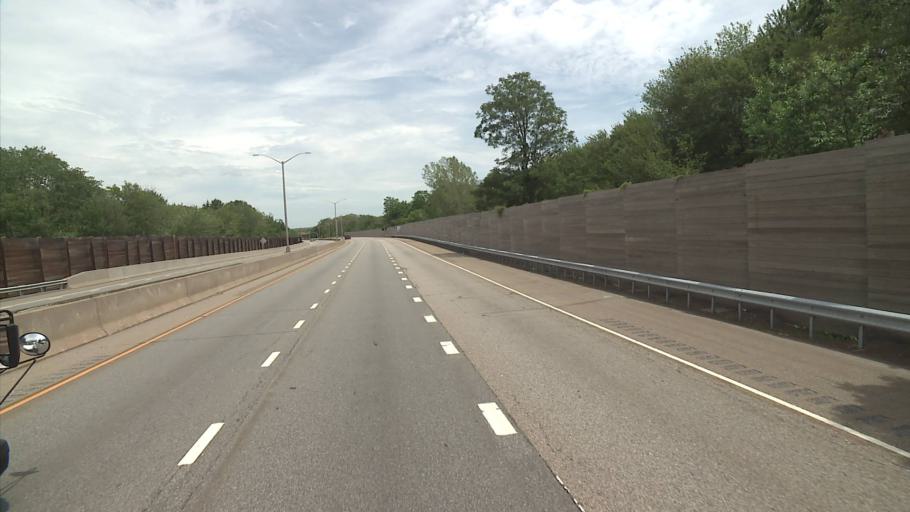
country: US
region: Connecticut
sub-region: New London County
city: Norwich
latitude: 41.4810
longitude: -72.0916
